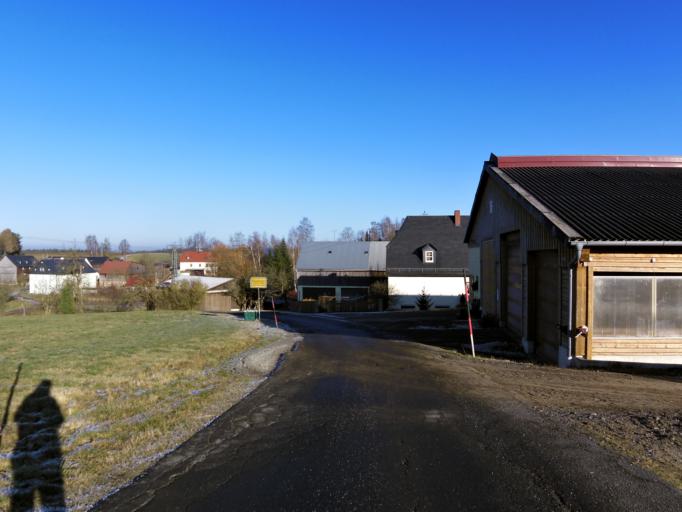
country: DE
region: Bavaria
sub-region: Upper Franconia
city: Roslau
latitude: 50.0843
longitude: 12.0299
